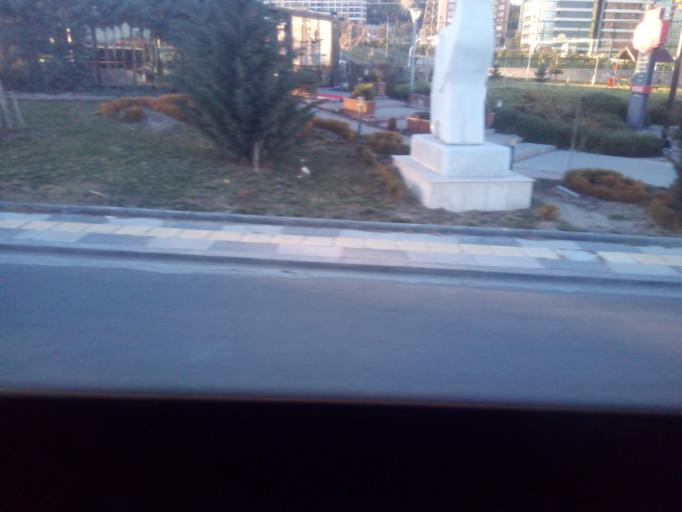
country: TR
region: Ankara
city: Etimesgut
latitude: 39.8817
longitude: 32.6587
